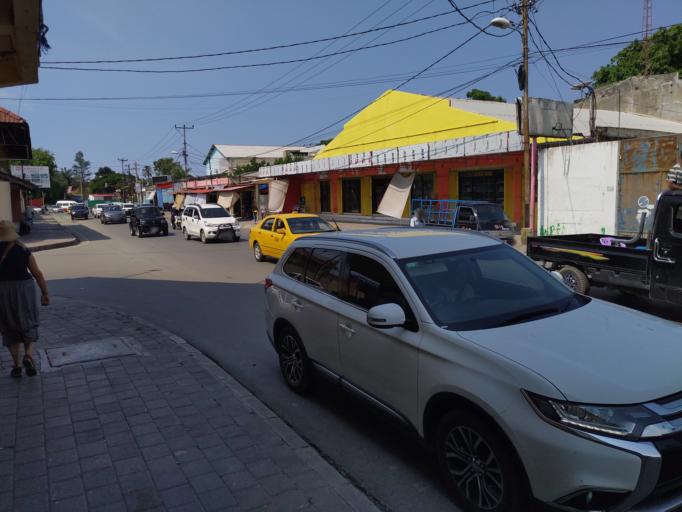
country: TL
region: Dili
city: Dili
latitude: -8.5553
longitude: 125.5717
